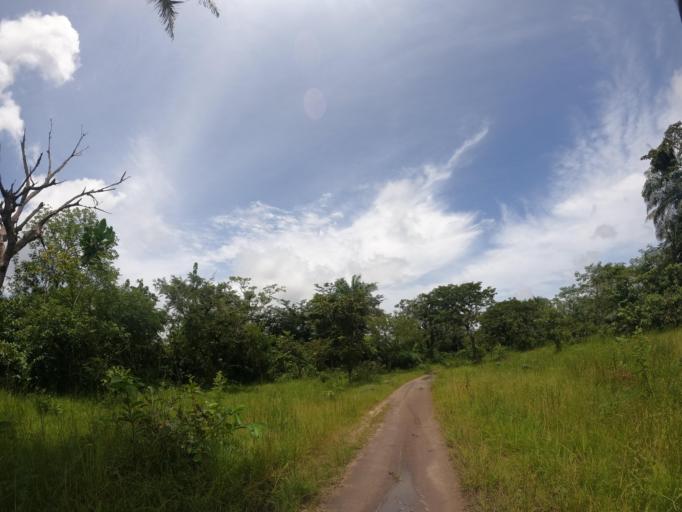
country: SL
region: Northern Province
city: Binkolo
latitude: 9.1423
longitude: -12.2417
